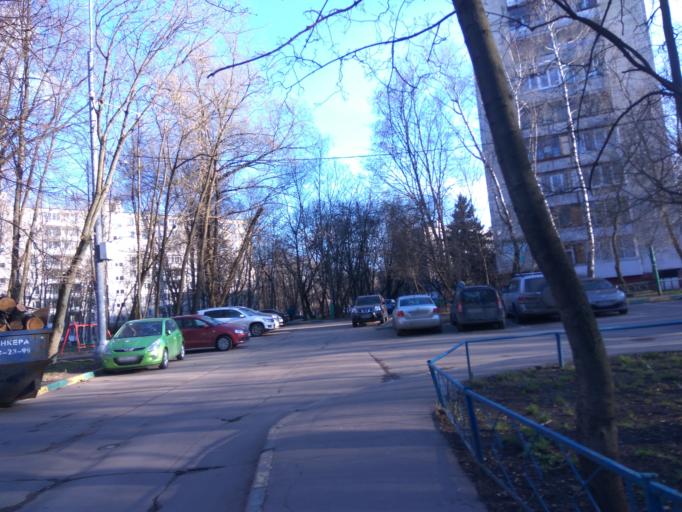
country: RU
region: Moscow
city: Veshnyaki
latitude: 55.7255
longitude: 37.8083
